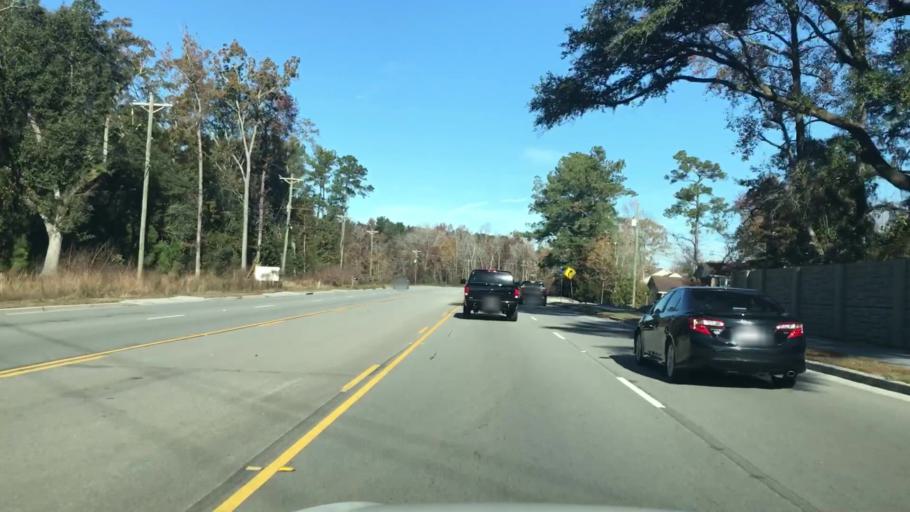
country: US
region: South Carolina
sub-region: Dorchester County
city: Centerville
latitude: 32.9623
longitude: -80.2013
